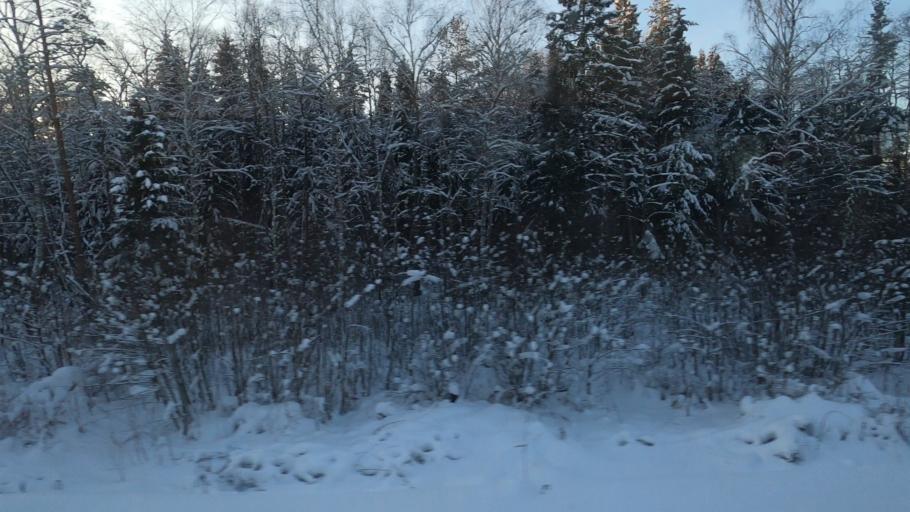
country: RU
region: Moskovskaya
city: Novo-Nikol'skoye
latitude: 56.6076
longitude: 37.5681
